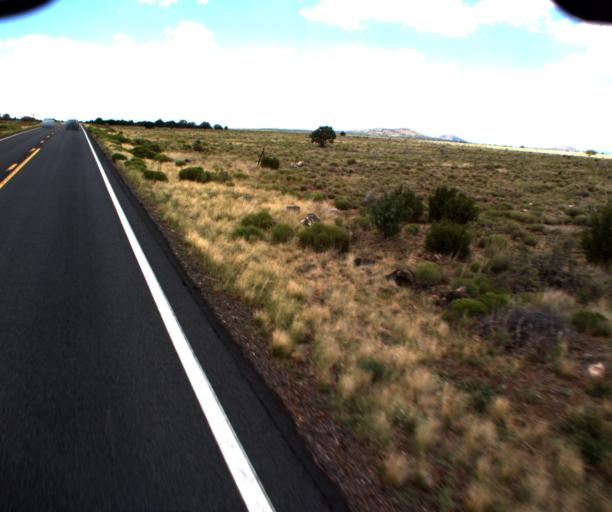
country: US
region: Arizona
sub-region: Coconino County
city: Parks
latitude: 35.5742
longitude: -111.9306
